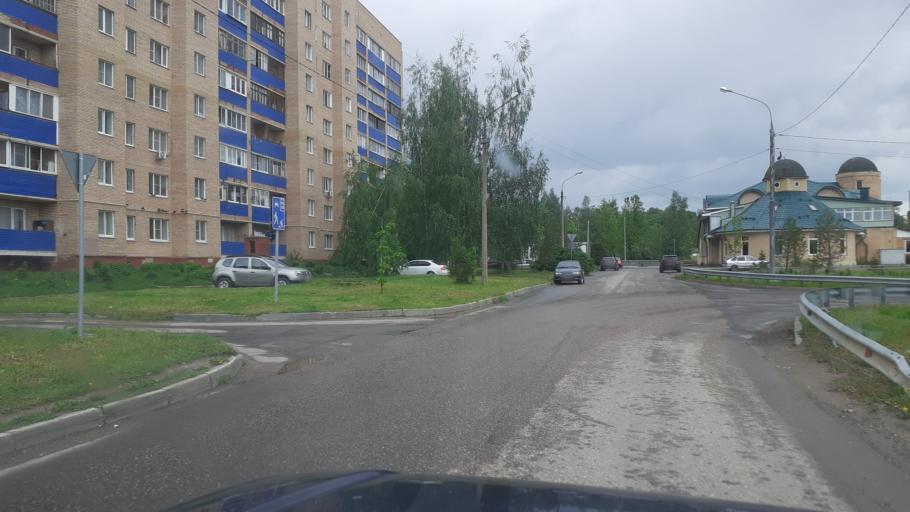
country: RU
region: Moskovskaya
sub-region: Volokolamskiy Rayon
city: Volokolamsk
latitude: 56.0271
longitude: 35.9464
